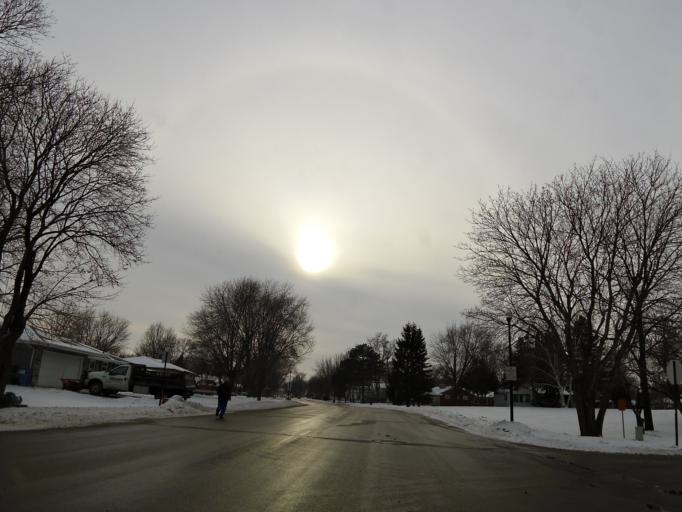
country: US
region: Minnesota
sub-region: McLeod County
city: Hutchinson
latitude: 44.9001
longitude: -94.3586
